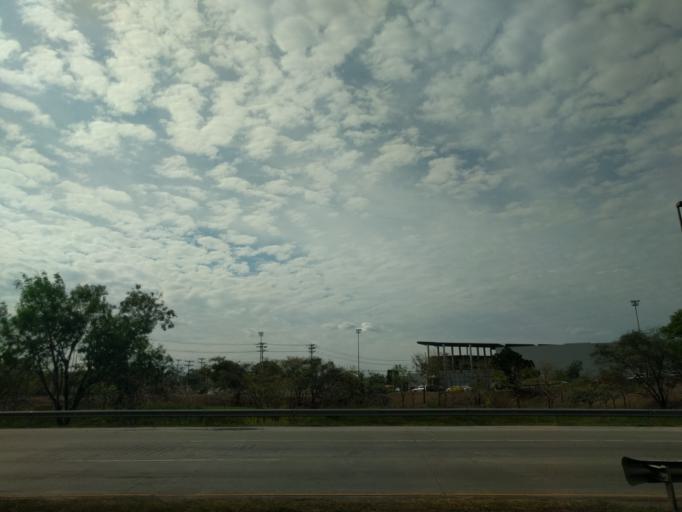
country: PA
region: Panama
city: San Miguelito
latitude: 9.0251
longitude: -79.4682
